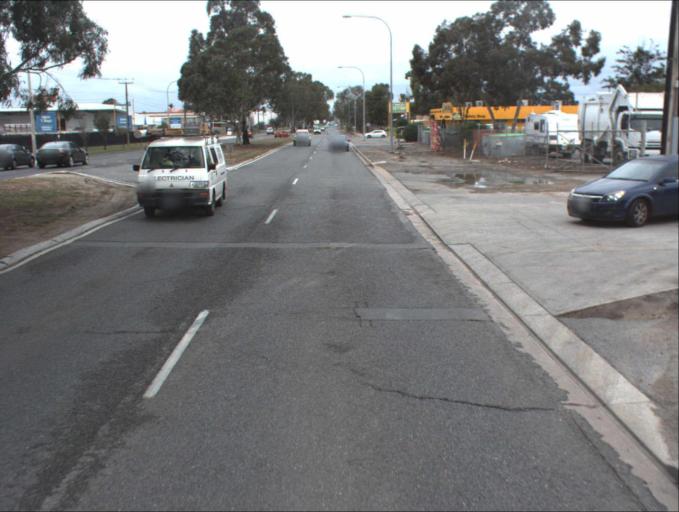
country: AU
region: South Australia
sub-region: Port Adelaide Enfield
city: Enfield
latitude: -34.8394
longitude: 138.5936
